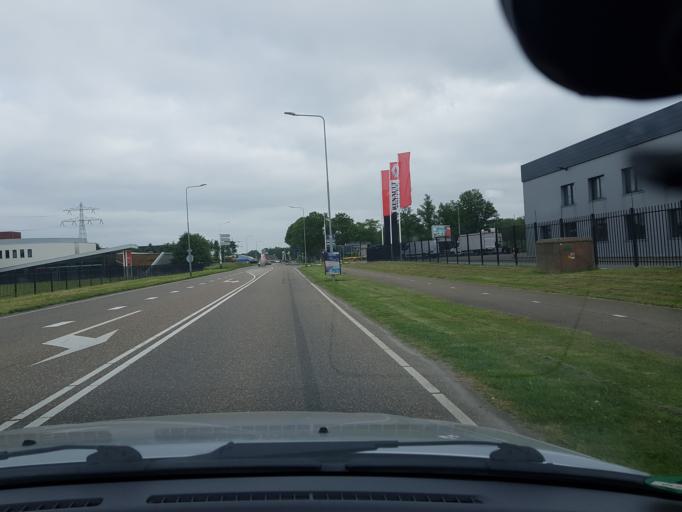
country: NL
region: Limburg
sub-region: Gemeente Stein
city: Elsloo
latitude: 50.9512
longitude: 5.7849
